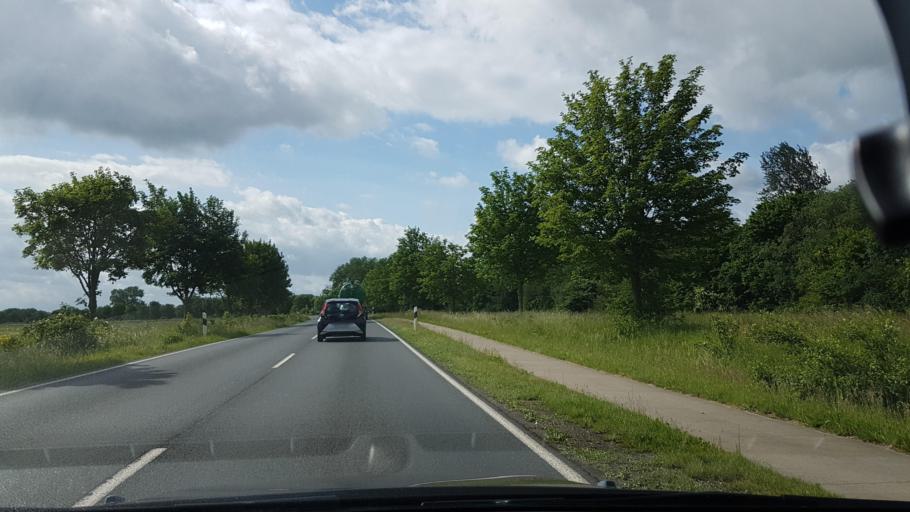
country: DE
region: Lower Saxony
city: Gehrden
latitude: 52.3132
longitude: 9.6224
